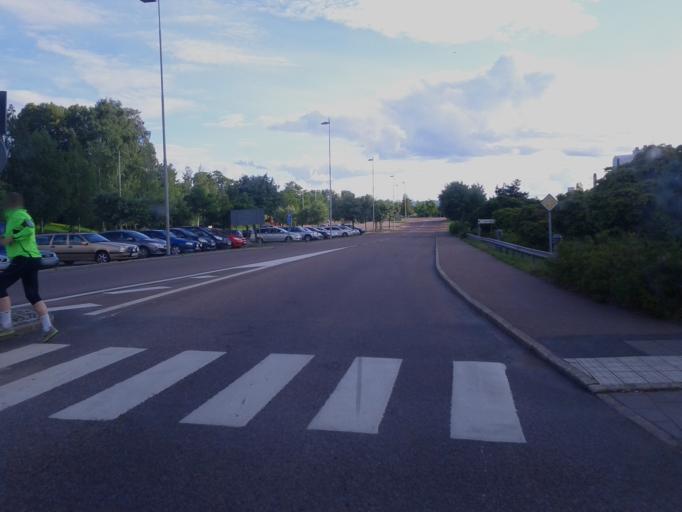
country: SE
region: Dalarna
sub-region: Borlange Kommun
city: Borlaenge
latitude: 60.4860
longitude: 15.4298
